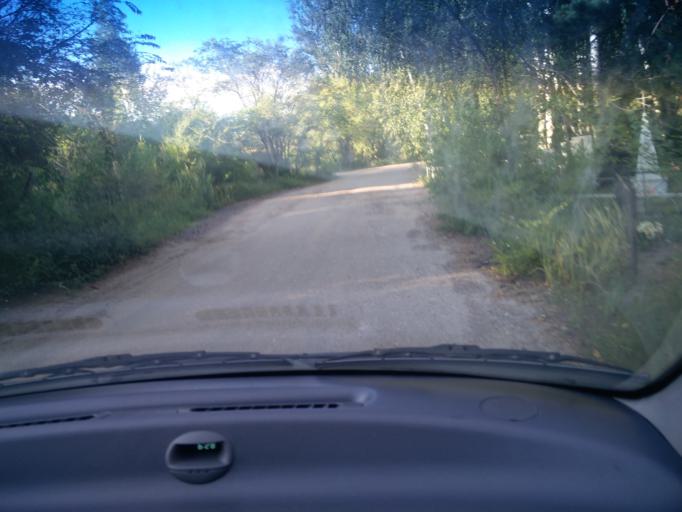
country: RU
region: Voronezj
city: Pridonskoy
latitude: 51.6734
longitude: 39.1093
